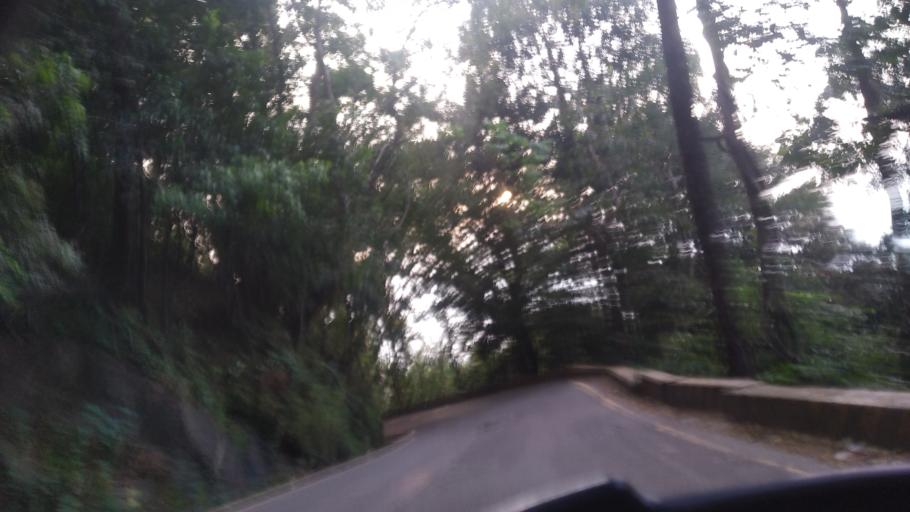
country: IN
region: Kerala
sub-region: Wayanad
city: Kalpetta
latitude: 11.4990
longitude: 76.0248
